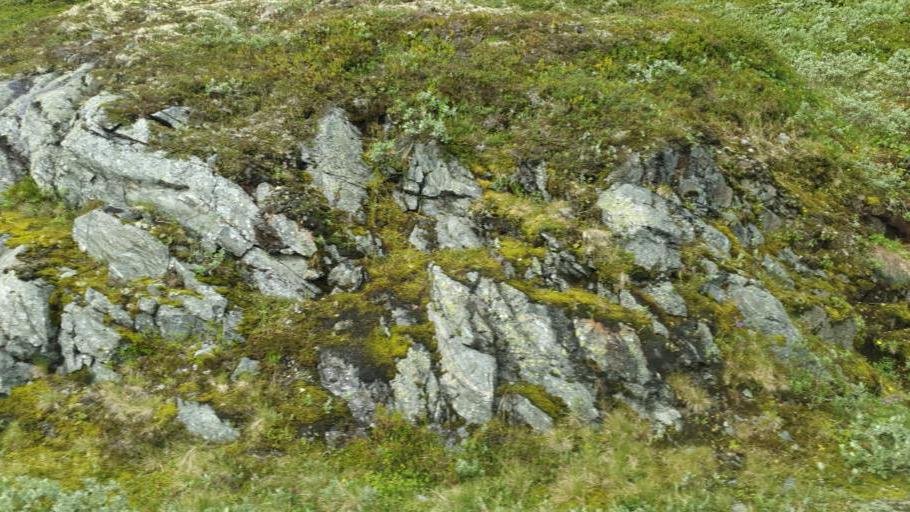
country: NO
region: Oppland
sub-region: Vestre Slidre
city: Slidre
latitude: 61.3395
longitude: 8.8150
